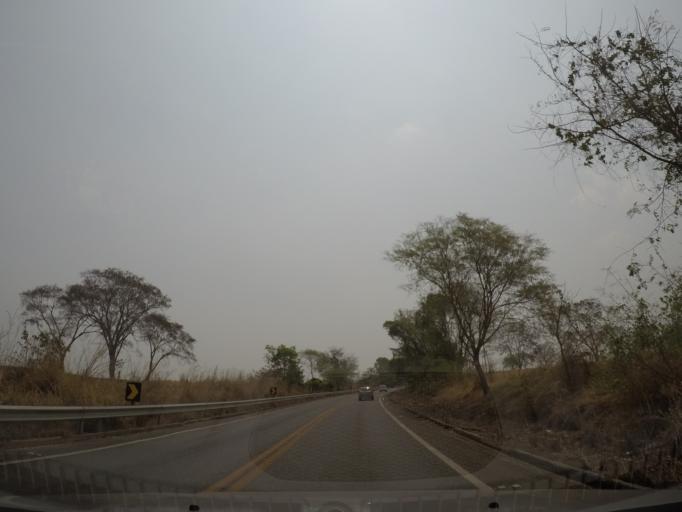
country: BR
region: Goias
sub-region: Pirenopolis
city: Pirenopolis
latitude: -15.8885
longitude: -48.8980
